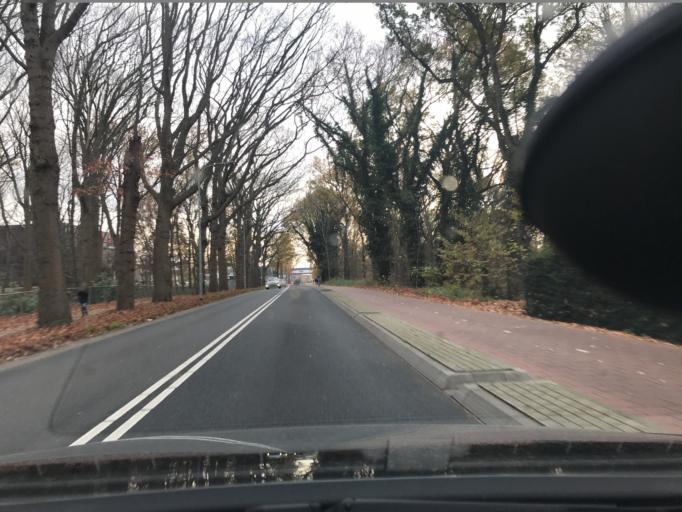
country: NL
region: Limburg
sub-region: Gemeente Venlo
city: Venlo
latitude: 51.3895
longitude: 6.1675
